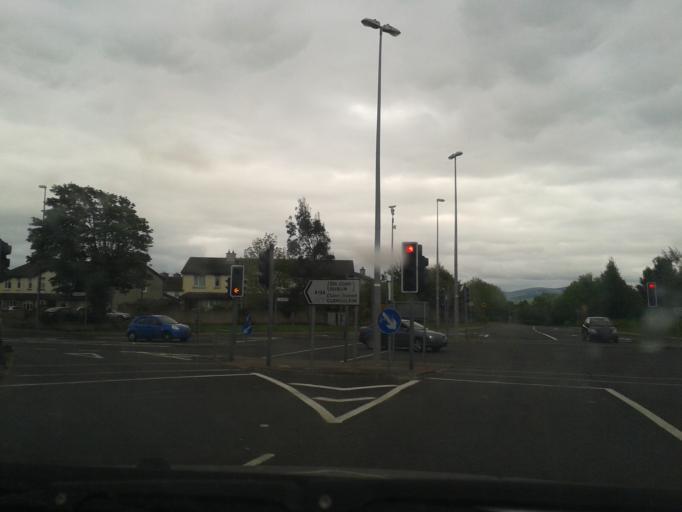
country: IE
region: Leinster
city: Clondalkin
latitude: 53.3208
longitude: -6.4222
